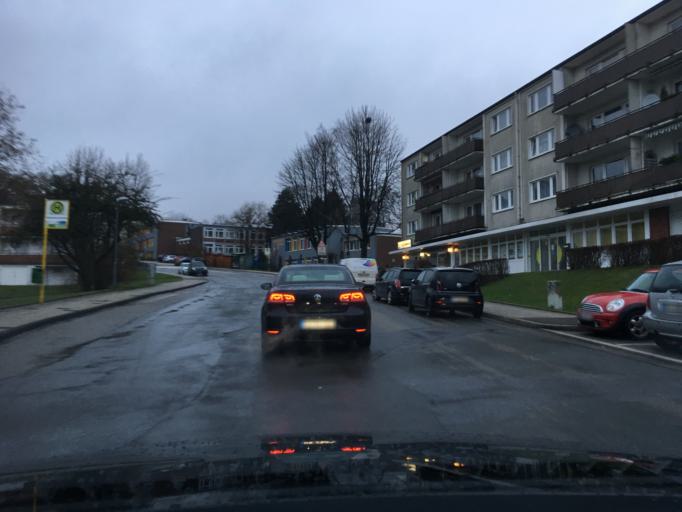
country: DE
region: North Rhine-Westphalia
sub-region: Regierungsbezirk Dusseldorf
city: Velbert
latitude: 51.3037
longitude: 7.1042
